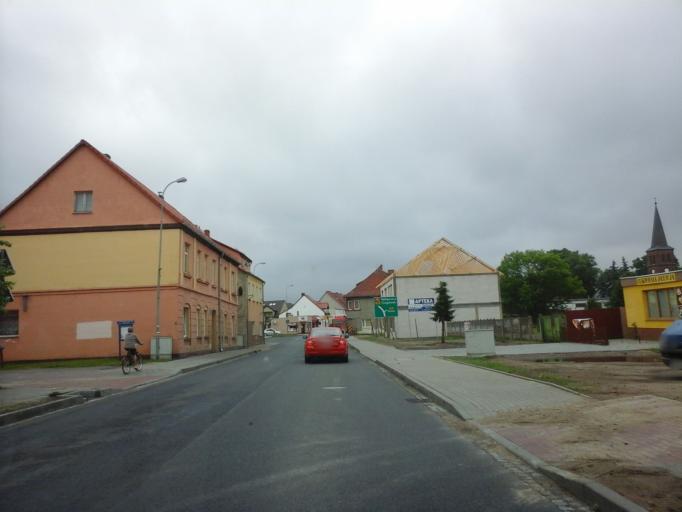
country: PL
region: West Pomeranian Voivodeship
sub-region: Powiat walecki
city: Miroslawiec
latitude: 53.3425
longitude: 16.0905
